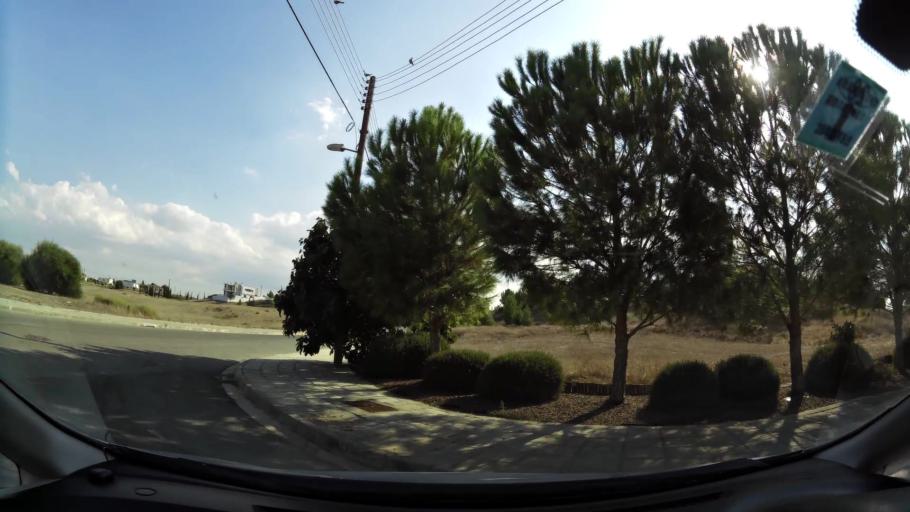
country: CY
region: Lefkosia
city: Kato Deftera
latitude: 35.1429
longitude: 33.2950
